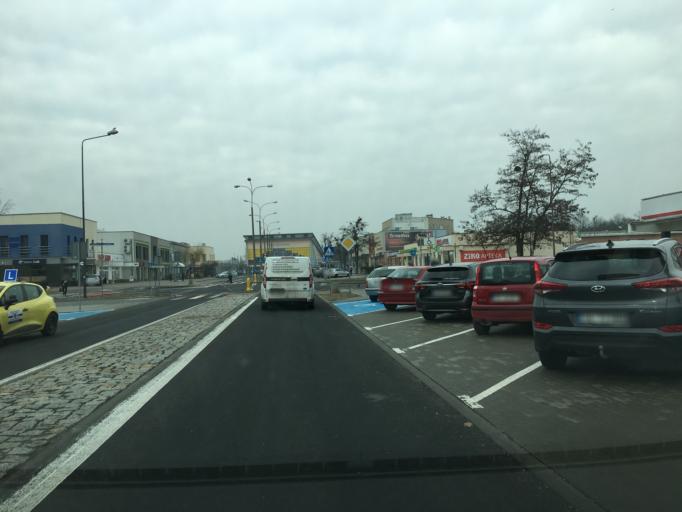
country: PL
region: Opole Voivodeship
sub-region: Powiat kedzierzynsko-kozielski
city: Kedzierzyn-Kozle
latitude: 50.3459
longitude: 18.2195
